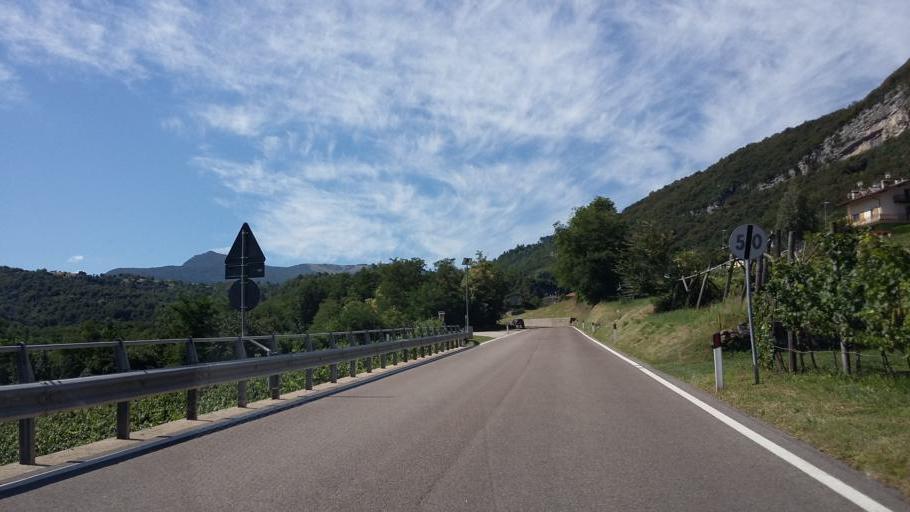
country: IT
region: Trentino-Alto Adige
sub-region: Provincia di Trento
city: Mori
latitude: 45.8421
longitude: 10.9720
